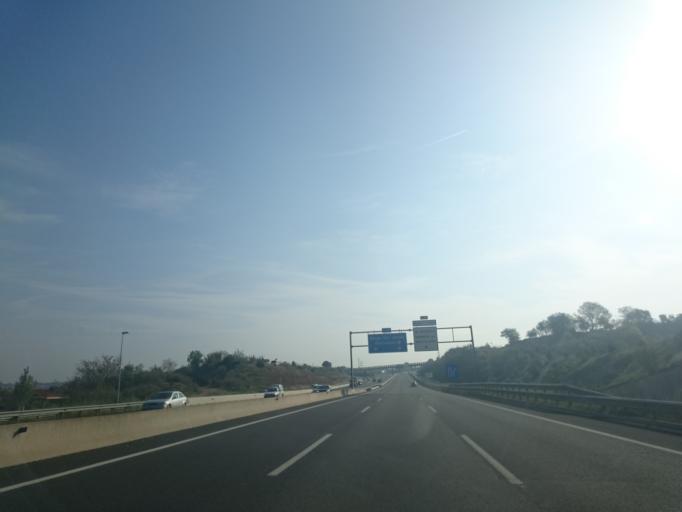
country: ES
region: Catalonia
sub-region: Provincia de Barcelona
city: Manresa
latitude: 41.7414
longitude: 1.8235
